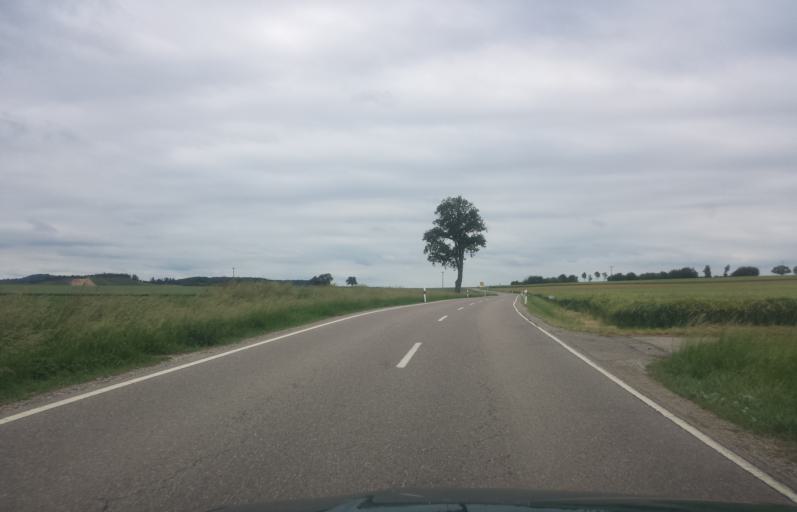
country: DE
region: Bavaria
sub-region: Regierungsbezirk Mittelfranken
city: Weigenheim
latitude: 49.5538
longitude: 10.2629
